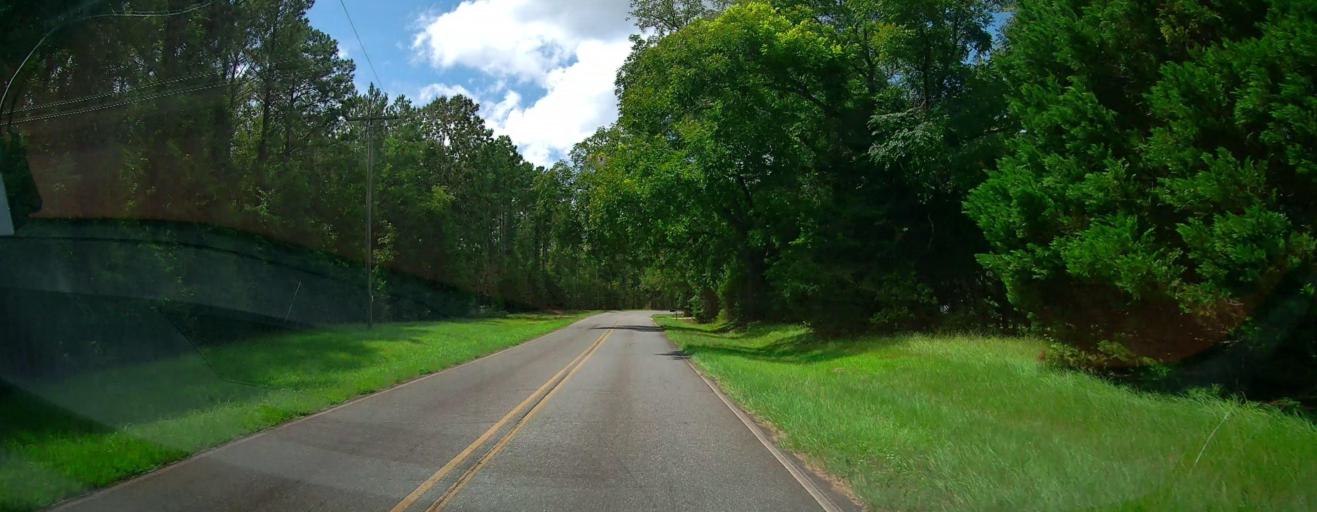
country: US
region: Georgia
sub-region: Houston County
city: Perry
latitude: 32.5112
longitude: -83.7449
